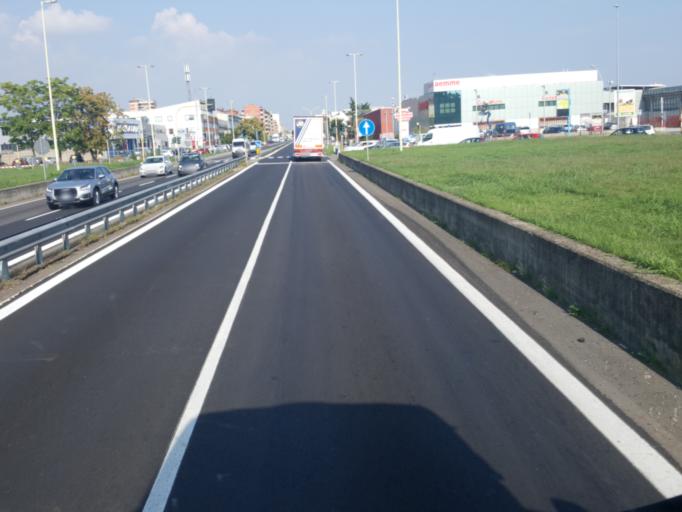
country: IT
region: Lombardy
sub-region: Citta metropolitana di Milano
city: Trezzano sul Naviglio
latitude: 45.4194
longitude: 9.0544
